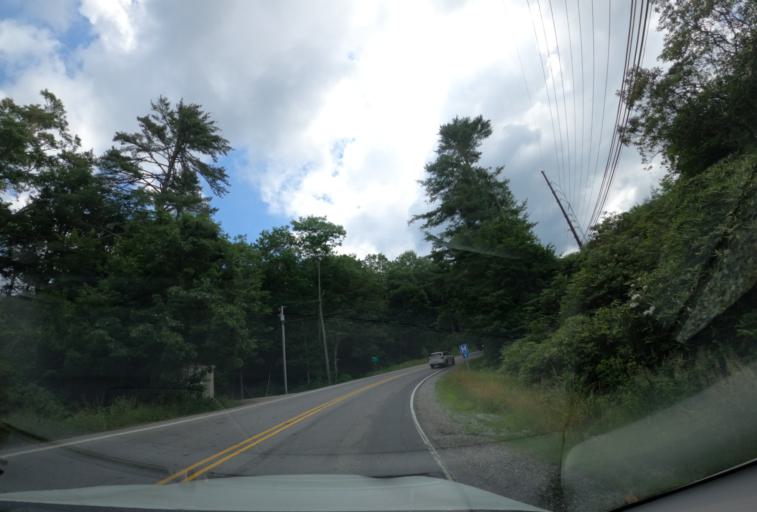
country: US
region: North Carolina
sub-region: Macon County
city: Franklin
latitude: 35.0830
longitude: -83.1888
